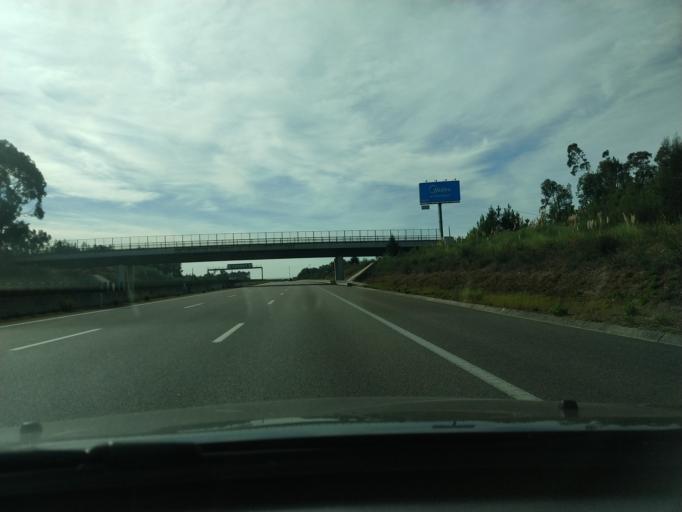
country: PT
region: Aveiro
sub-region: Santa Maria da Feira
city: Feira
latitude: 40.9124
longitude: -8.5680
